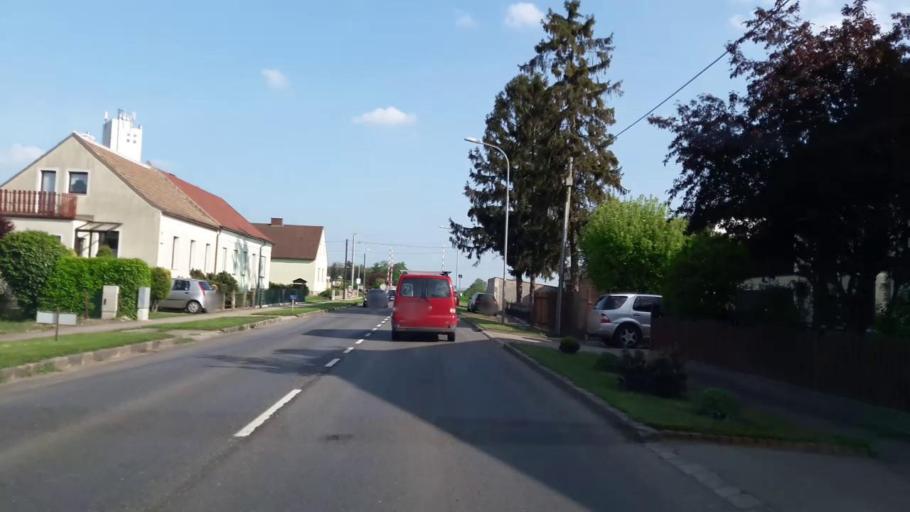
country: AT
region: Lower Austria
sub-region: Politischer Bezirk Hollabrunn
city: Guntersdorf
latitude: 48.6442
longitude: 16.0490
